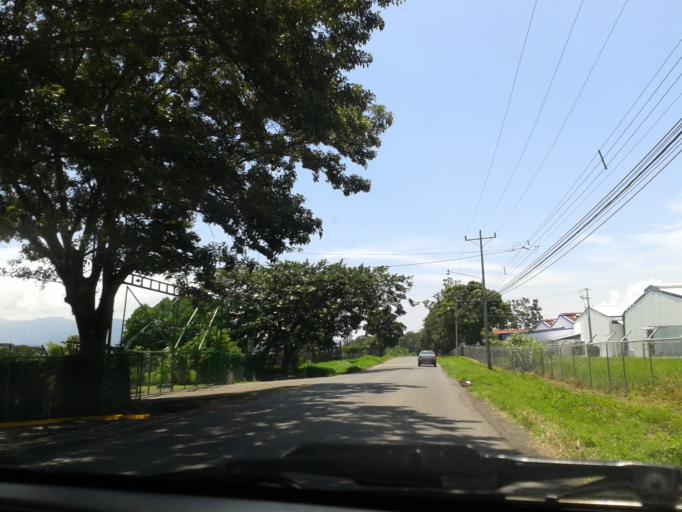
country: CR
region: Alajuela
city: Alajuela
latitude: 10.0030
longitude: -84.2338
